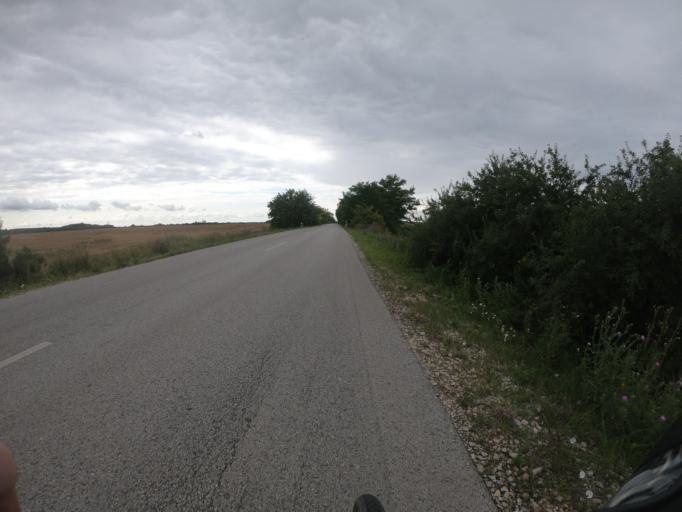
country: HU
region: Heves
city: Poroszlo
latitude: 47.6969
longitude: 20.7237
